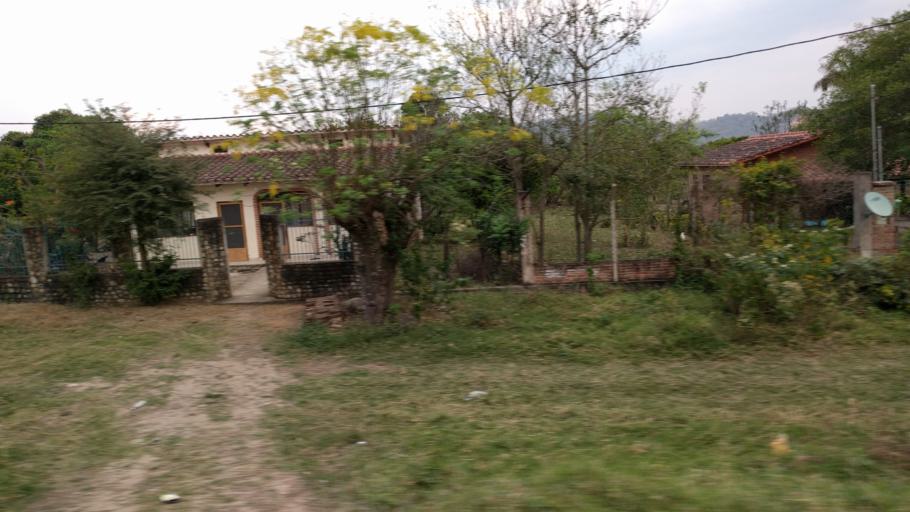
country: BO
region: Santa Cruz
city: Jorochito
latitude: -18.1359
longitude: -63.4744
